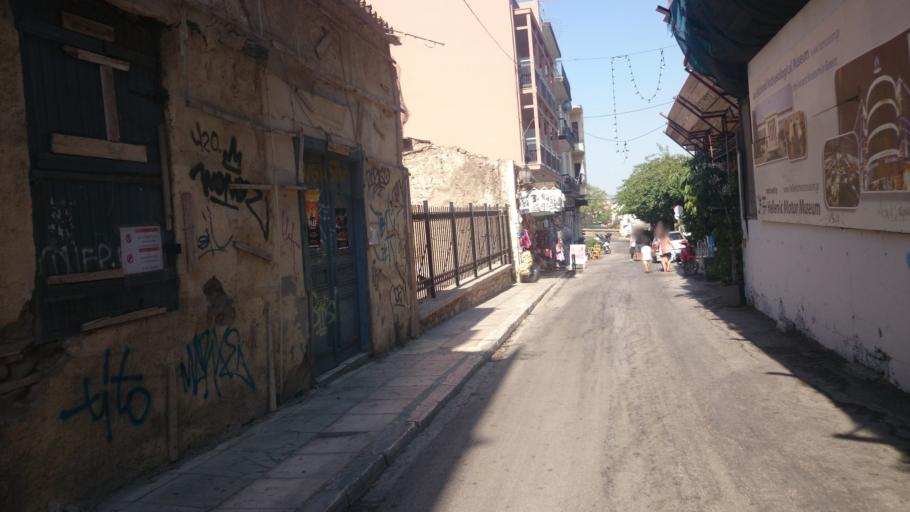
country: GR
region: Attica
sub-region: Nomarchia Athinas
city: Athens
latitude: 37.9746
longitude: 23.7282
